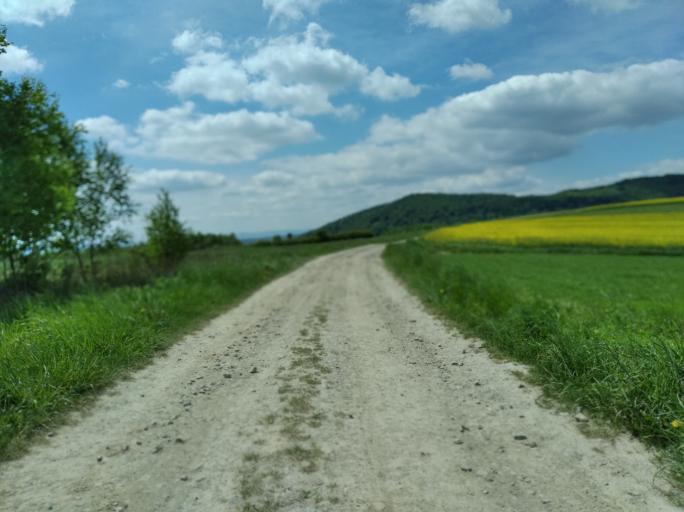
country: PL
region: Subcarpathian Voivodeship
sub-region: Powiat ropczycko-sedziszowski
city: Wielopole Skrzynskie
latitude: 49.8973
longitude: 21.5790
